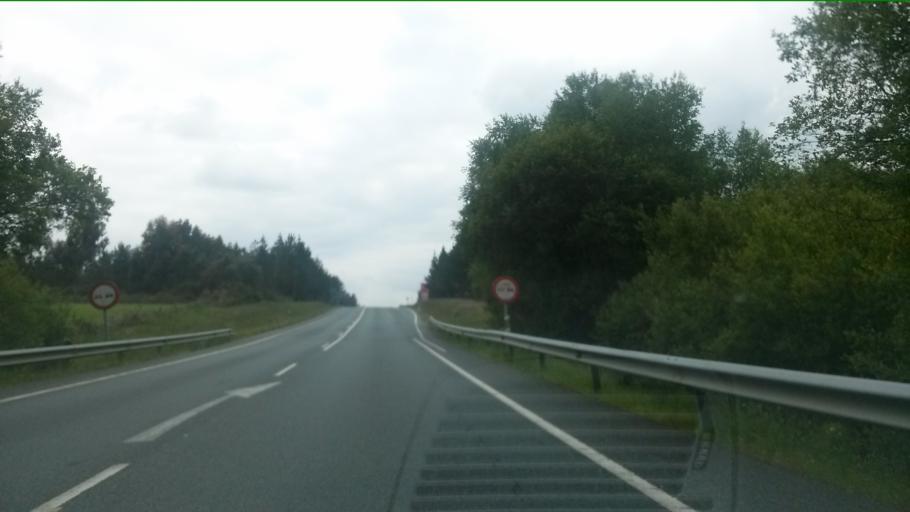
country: ES
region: Galicia
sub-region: Provincia de Lugo
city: Guitiriz
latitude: 43.1829
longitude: -7.9651
